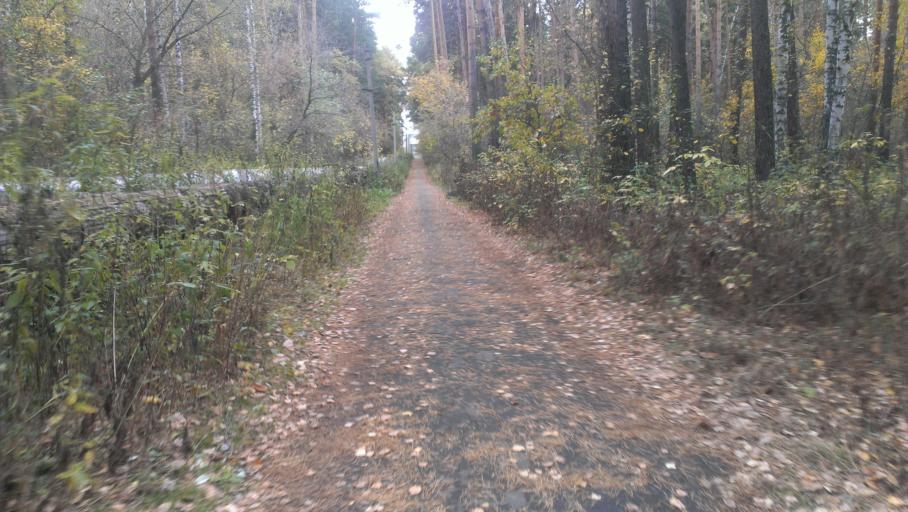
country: RU
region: Altai Krai
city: Yuzhnyy
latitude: 53.2611
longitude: 83.6879
